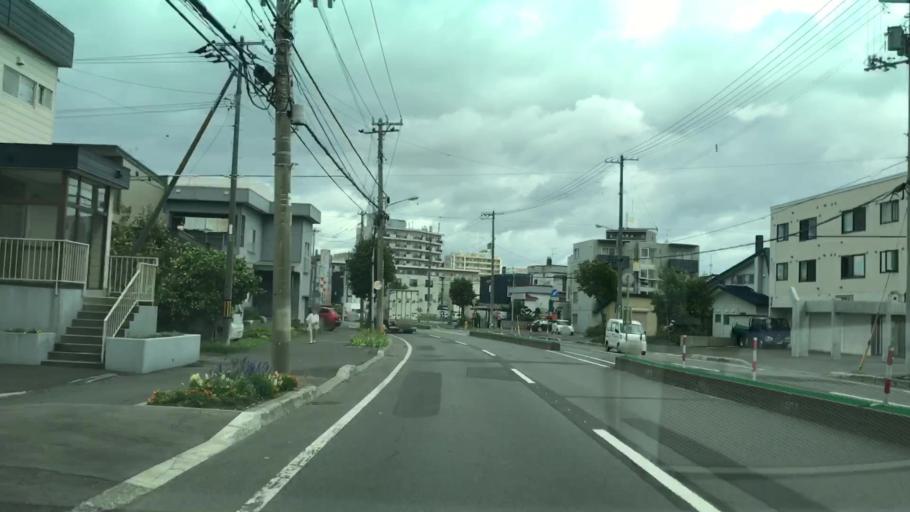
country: JP
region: Hokkaido
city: Sapporo
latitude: 42.9944
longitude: 141.4413
